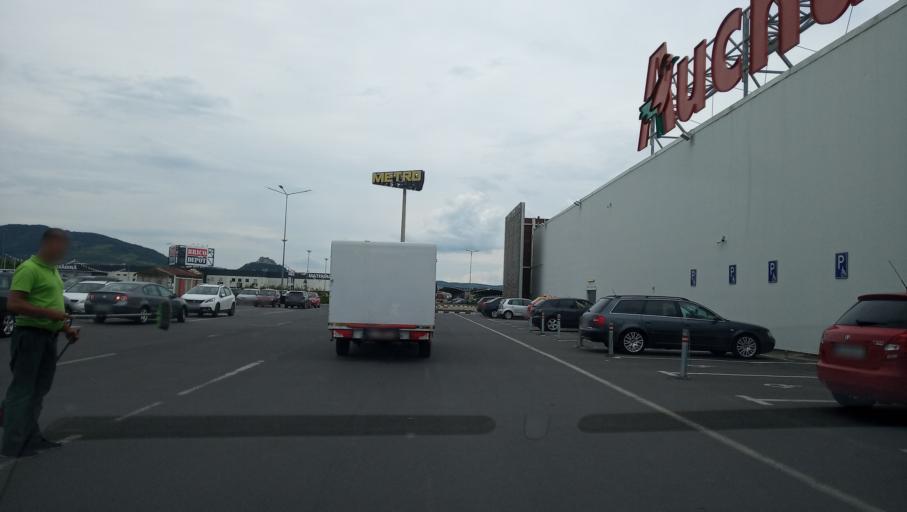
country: RO
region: Hunedoara
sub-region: Municipiul Deva
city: Deva
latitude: 45.8622
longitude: 22.9283
